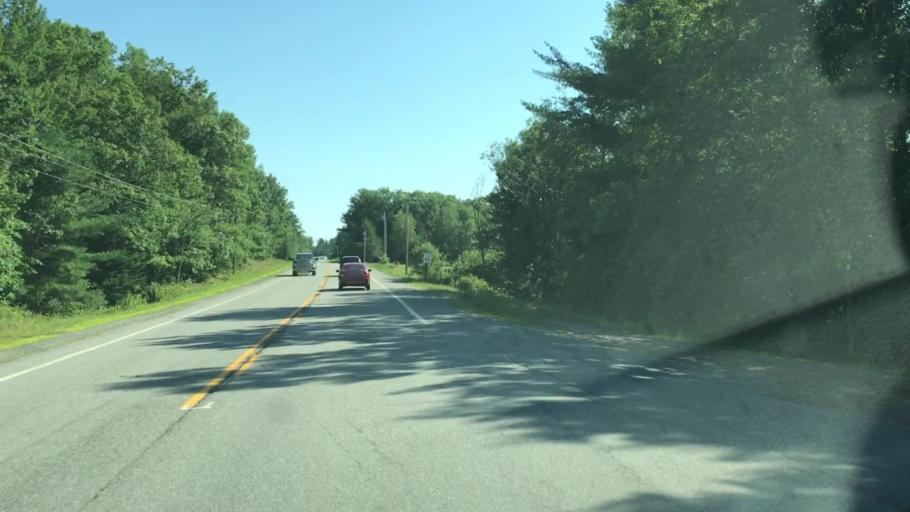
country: US
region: Maine
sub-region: Penobscot County
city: Enfield
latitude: 45.2951
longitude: -68.6209
